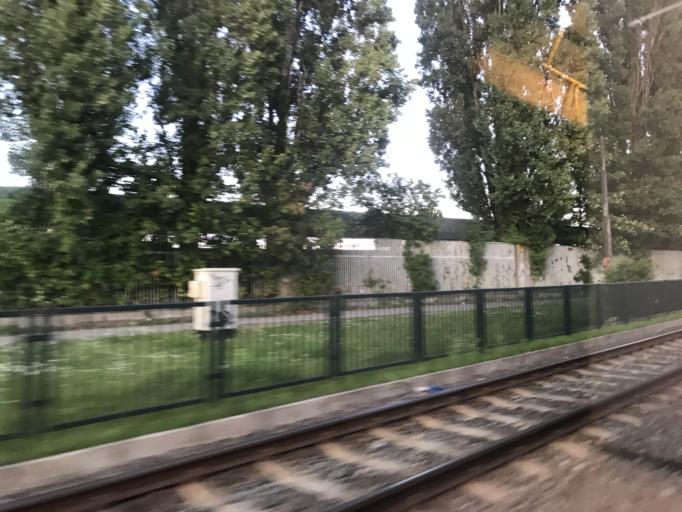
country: PL
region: Pomeranian Voivodeship
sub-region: Gdansk
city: Gdansk
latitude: 54.3737
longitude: 18.6318
